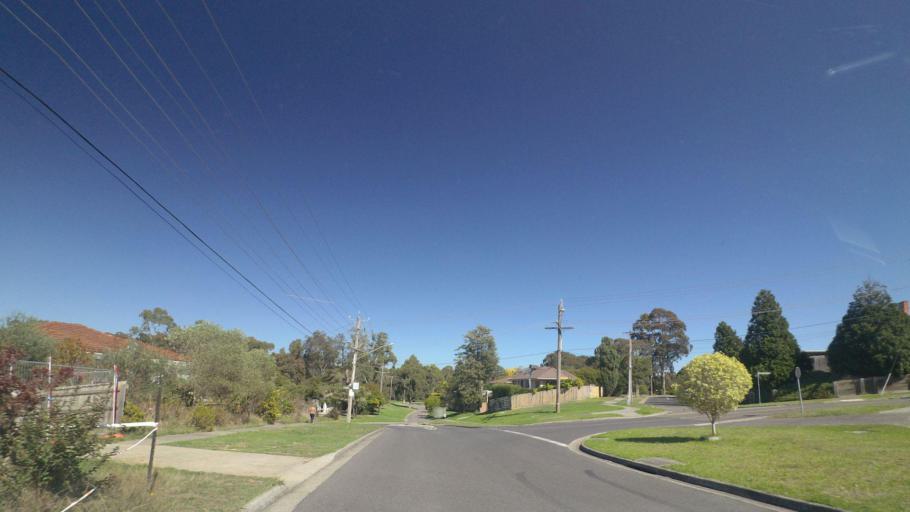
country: AU
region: Victoria
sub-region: Manningham
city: Donvale
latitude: -37.8007
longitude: 145.1690
